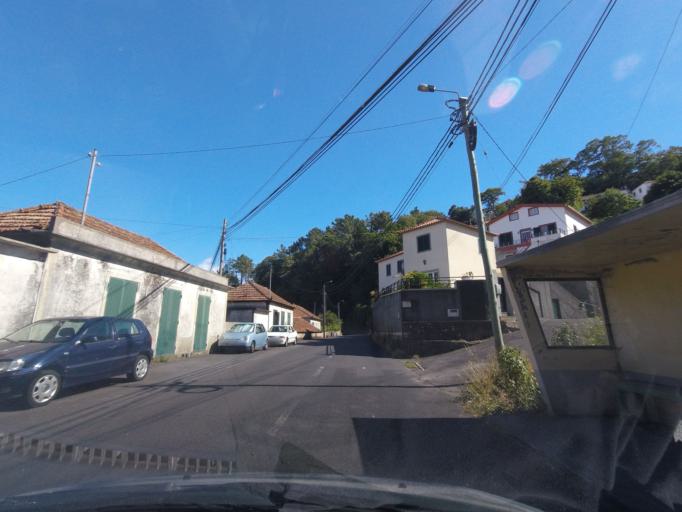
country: PT
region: Madeira
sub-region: Santa Cruz
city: Camacha
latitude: 32.6871
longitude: -16.8526
